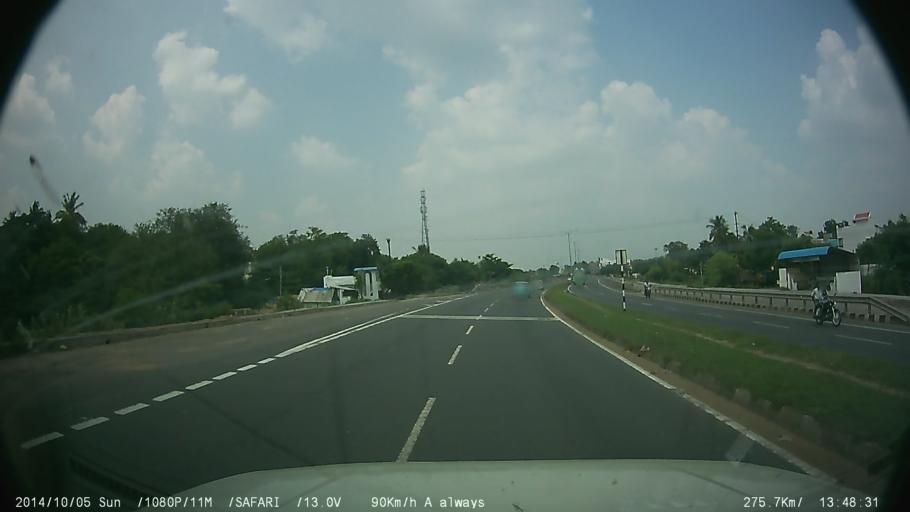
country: IN
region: Tamil Nadu
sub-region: Villupuram
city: Vikravandi
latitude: 12.0383
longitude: 79.5421
